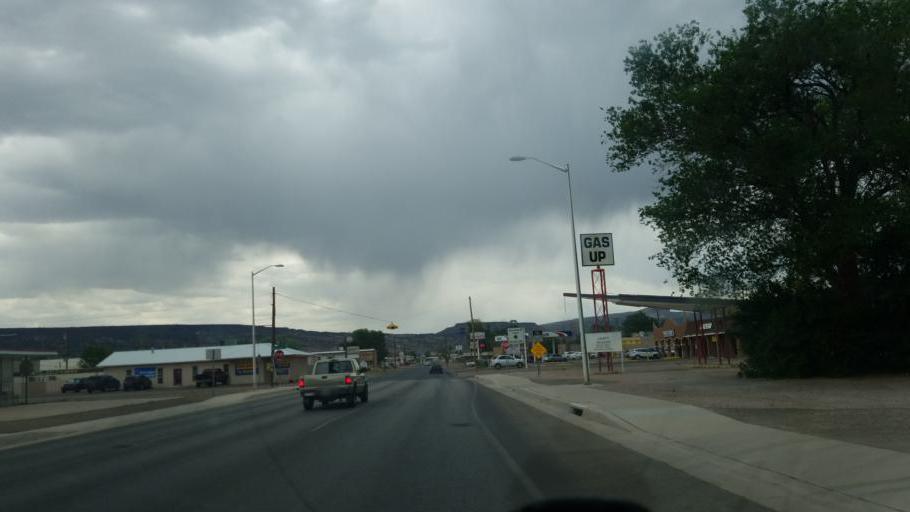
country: US
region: New Mexico
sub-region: Cibola County
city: Grants
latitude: 35.1547
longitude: -107.8460
